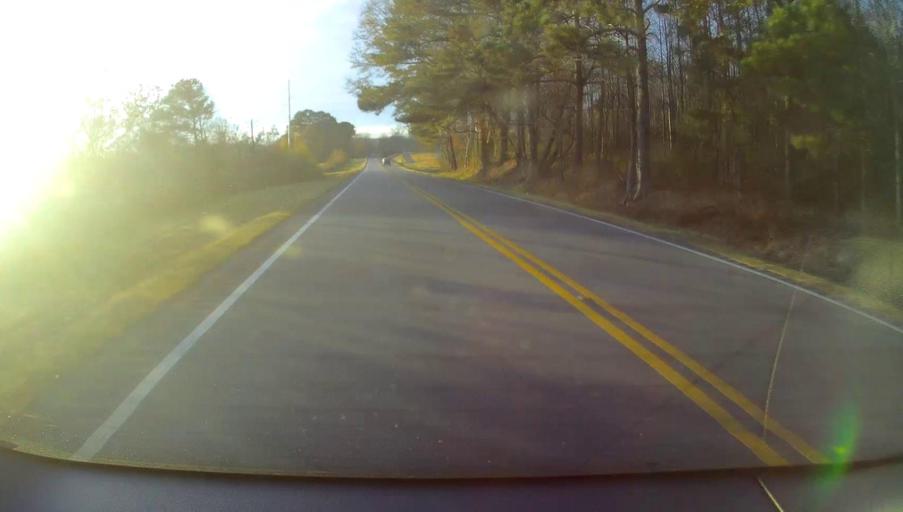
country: US
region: Alabama
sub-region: Saint Clair County
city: Steele
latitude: 34.0560
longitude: -86.2111
